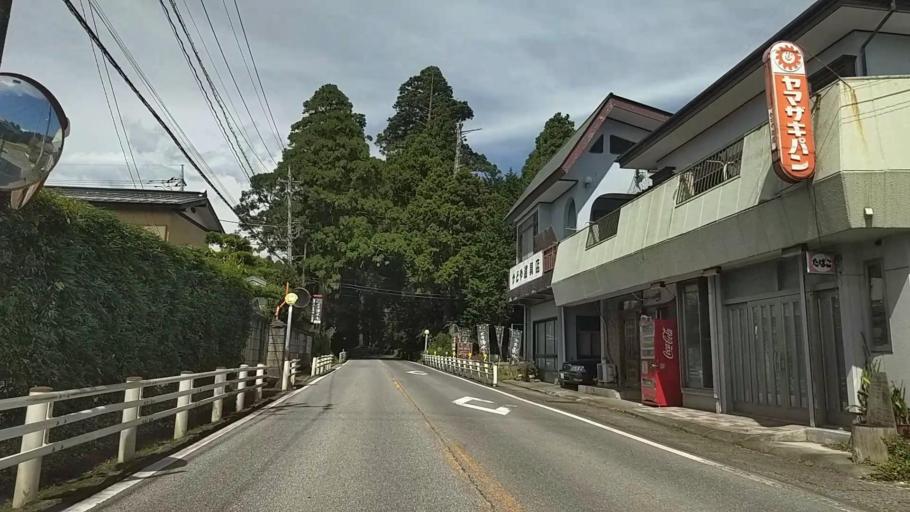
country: JP
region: Tochigi
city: Imaichi
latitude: 36.7083
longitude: 139.7448
